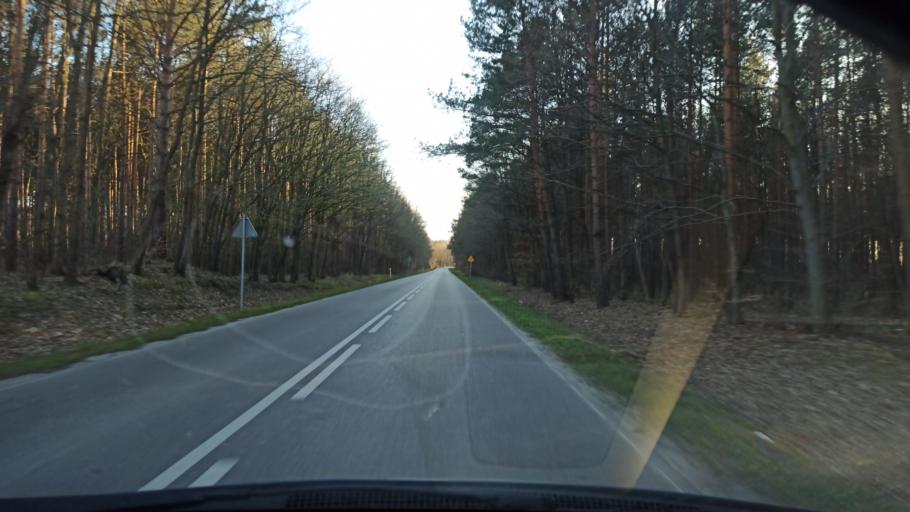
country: PL
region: Warmian-Masurian Voivodeship
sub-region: Powiat elblaski
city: Tolkmicko
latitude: 54.3022
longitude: 19.5040
